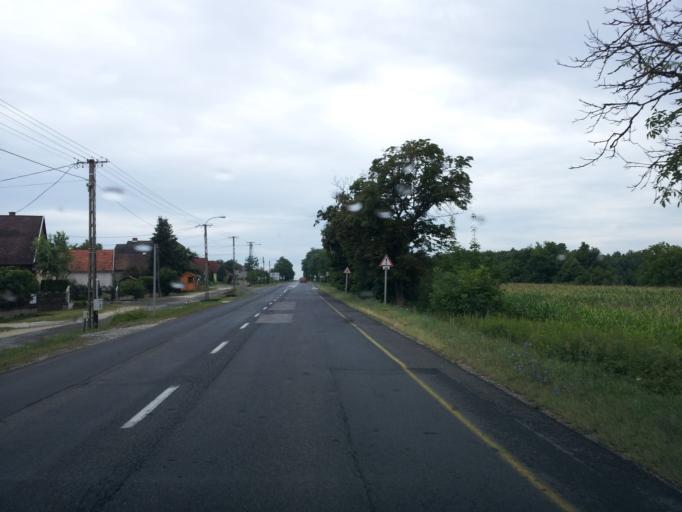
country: HU
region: Vas
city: Kormend
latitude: 46.9618
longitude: 16.6041
